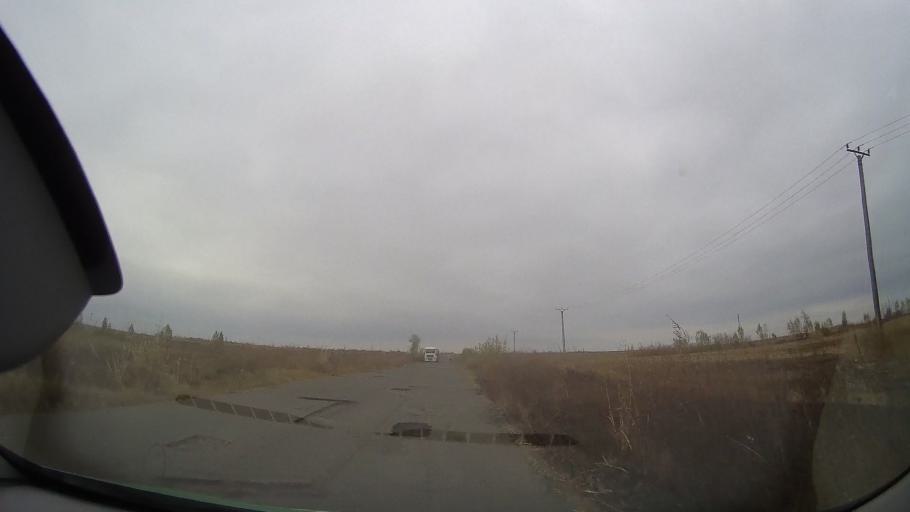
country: RO
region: Braila
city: Dudesti
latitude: 44.9295
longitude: 27.4275
